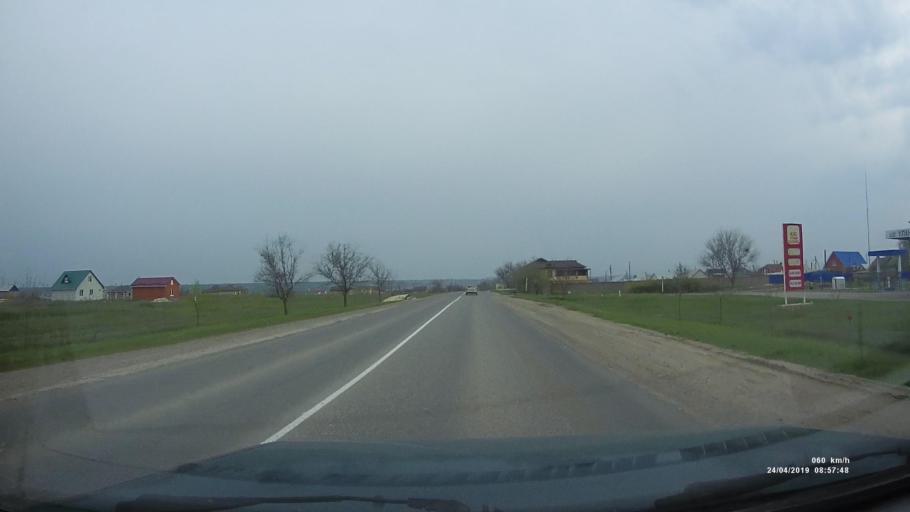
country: RU
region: Kalmykiya
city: Arshan'
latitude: 46.3045
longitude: 44.1908
